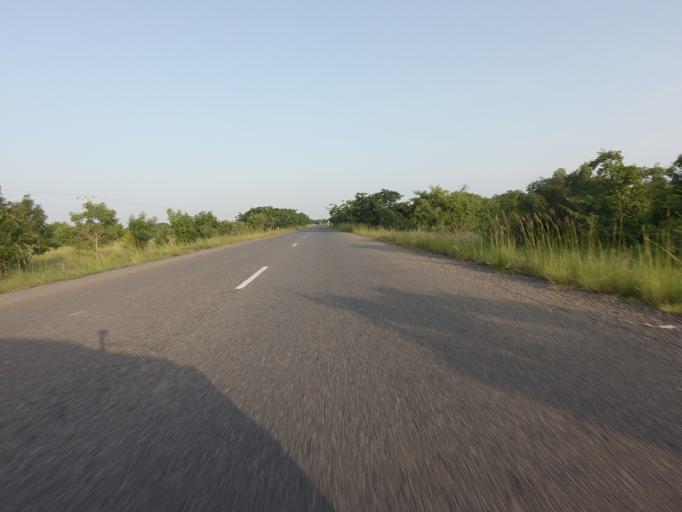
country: GH
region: Volta
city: Anloga
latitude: 5.9561
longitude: 0.6695
